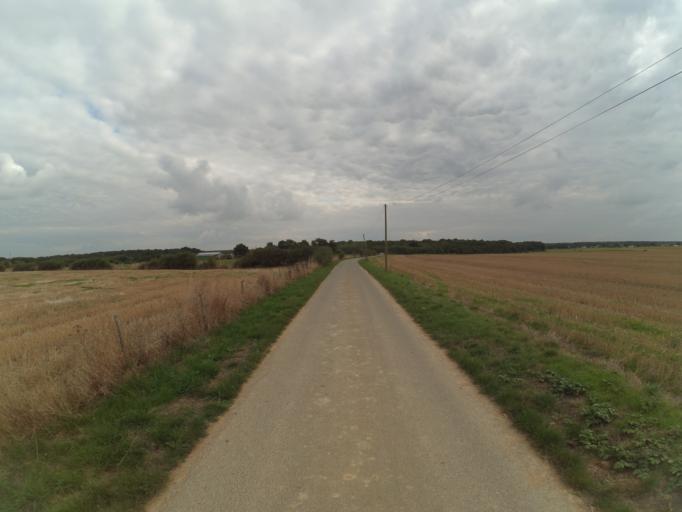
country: FR
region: Centre
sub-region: Departement d'Indre-et-Loire
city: Poce-sur-Cisse
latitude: 47.4859
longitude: 0.9693
